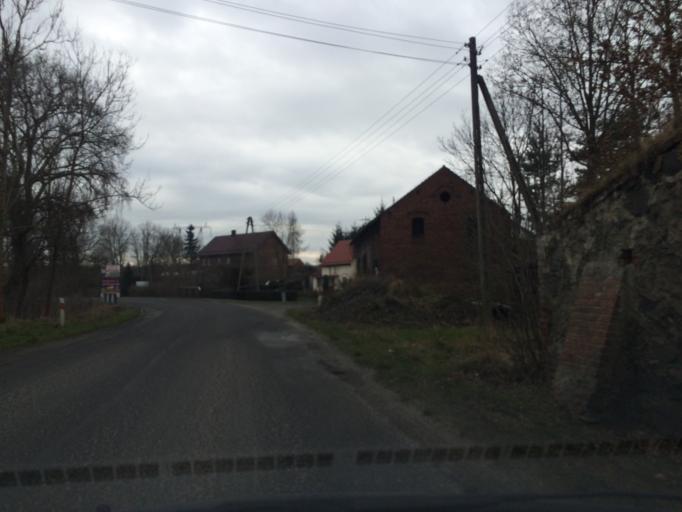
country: PL
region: Lower Silesian Voivodeship
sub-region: Powiat lubanski
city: Luban
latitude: 51.1444
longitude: 15.3120
